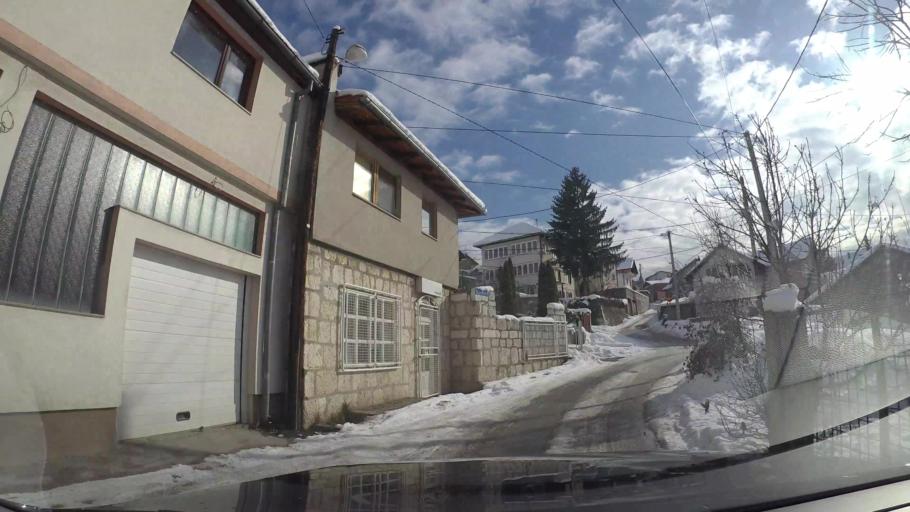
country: BA
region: Federation of Bosnia and Herzegovina
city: Kobilja Glava
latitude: 43.8749
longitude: 18.4194
